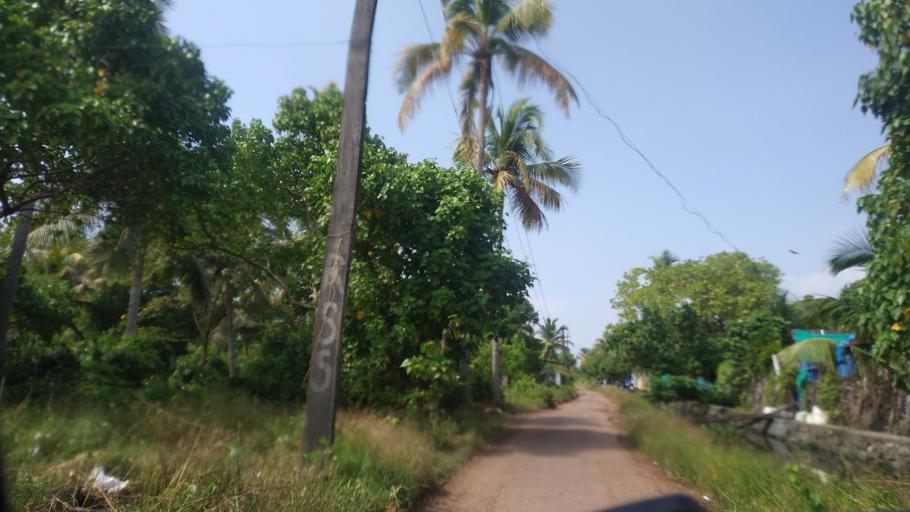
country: IN
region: Kerala
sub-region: Ernakulam
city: Elur
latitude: 10.0799
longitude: 76.2040
